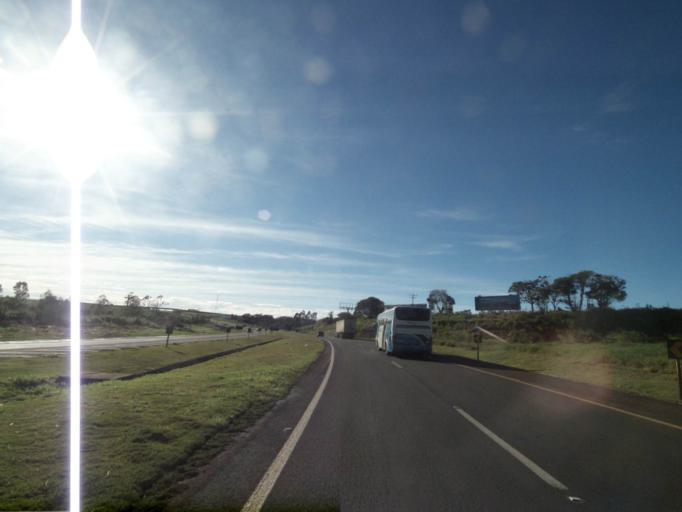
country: BR
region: Parana
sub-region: Cascavel
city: Cascavel
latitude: -25.0281
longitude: -53.5581
